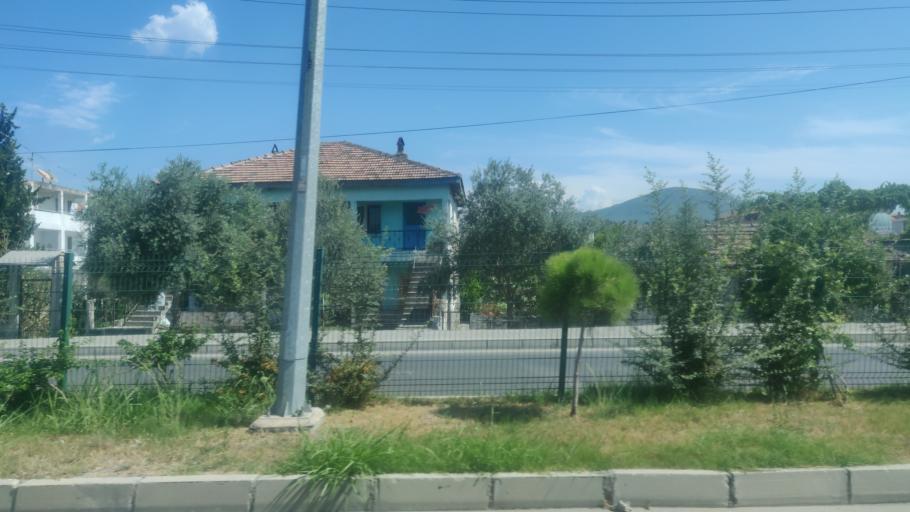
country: TR
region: Mugla
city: Dalaman
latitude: 36.7751
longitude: 28.8006
